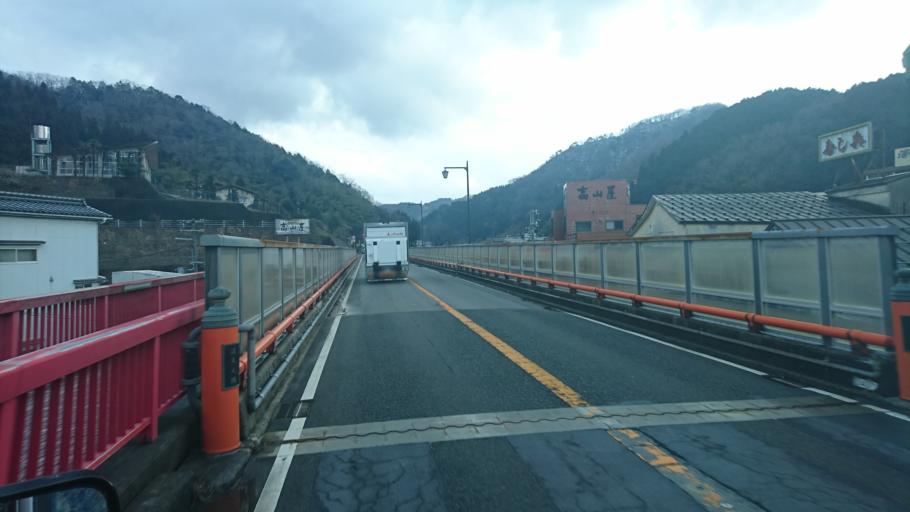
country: JP
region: Tottori
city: Tottori
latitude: 35.5557
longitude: 134.4900
